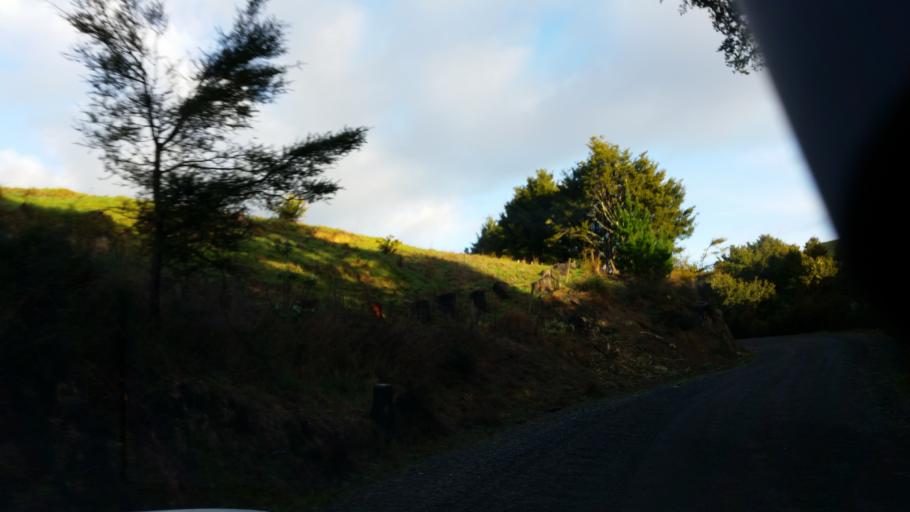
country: NZ
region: Northland
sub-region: Whangarei
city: Maungatapere
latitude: -35.7787
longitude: 174.0966
